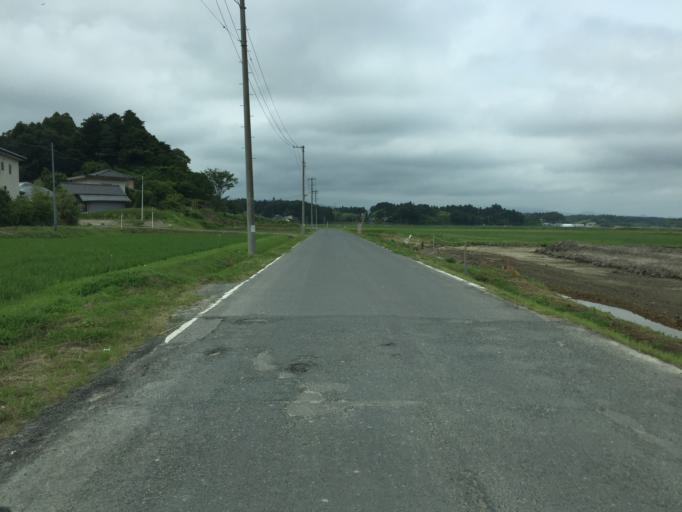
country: JP
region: Fukushima
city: Namie
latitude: 37.7301
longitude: 140.9824
